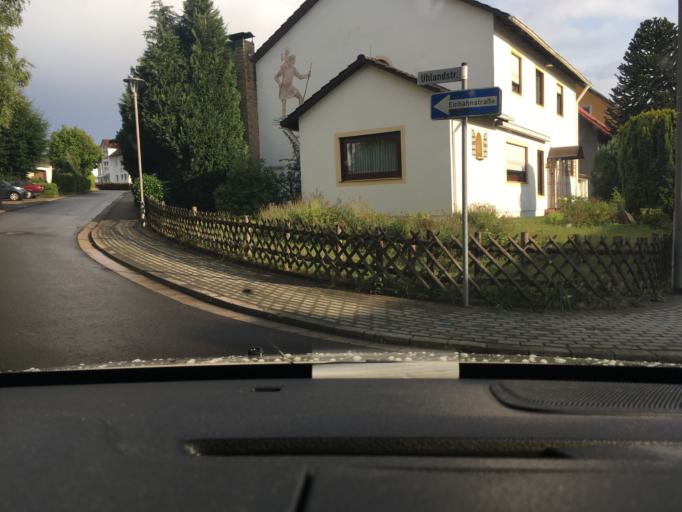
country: DE
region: Saarland
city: Sankt Ingbert
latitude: 49.2723
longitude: 7.1193
